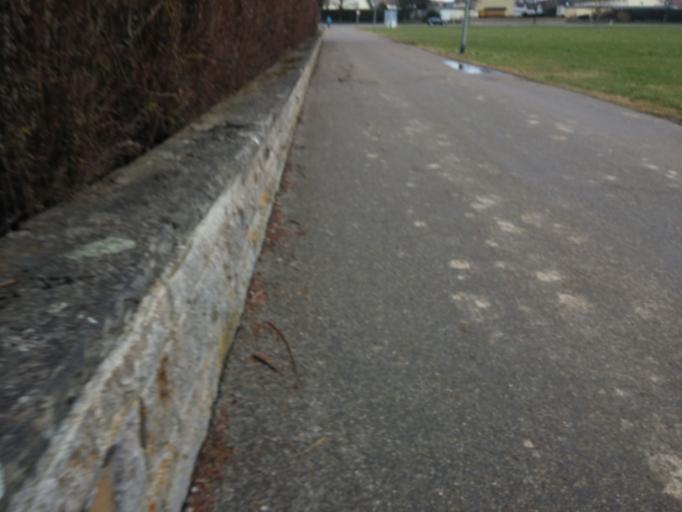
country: DE
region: Bavaria
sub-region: Swabia
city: Buxheim
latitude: 47.9936
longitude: 10.1557
